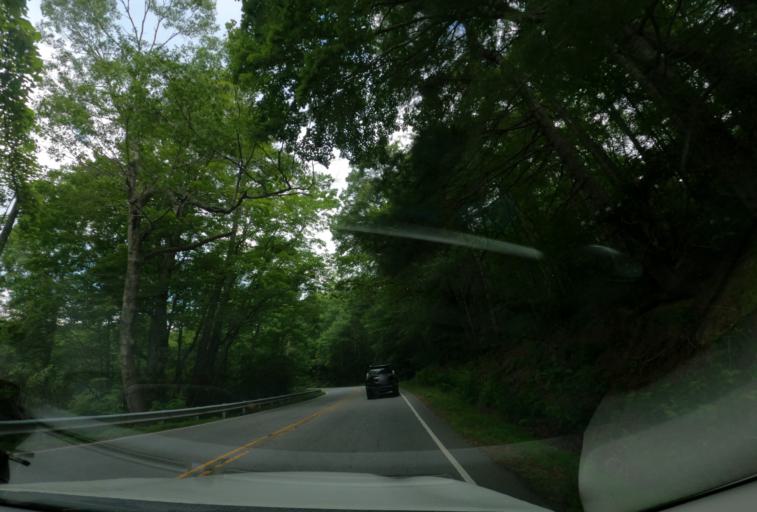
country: US
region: North Carolina
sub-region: Jackson County
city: Cullowhee
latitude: 35.1091
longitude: -83.1435
